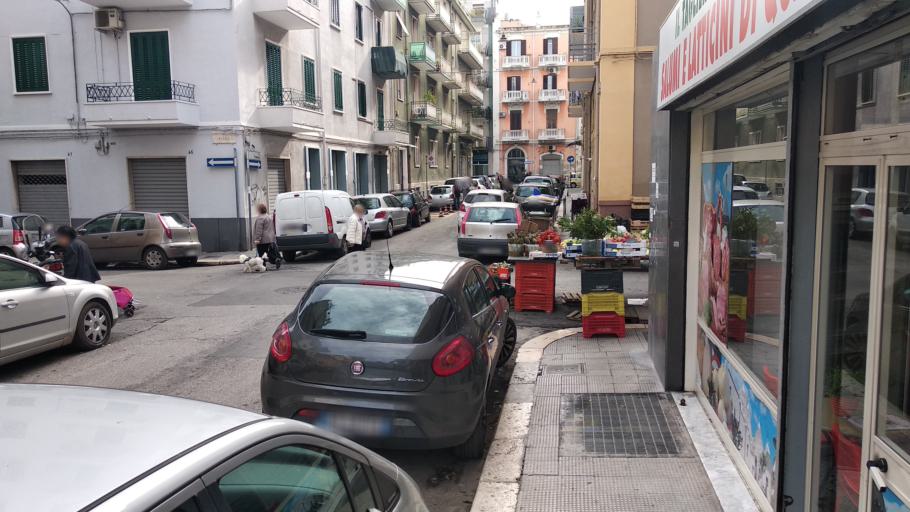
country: IT
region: Apulia
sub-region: Provincia di Bari
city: Bari
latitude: 41.1155
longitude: 16.8764
